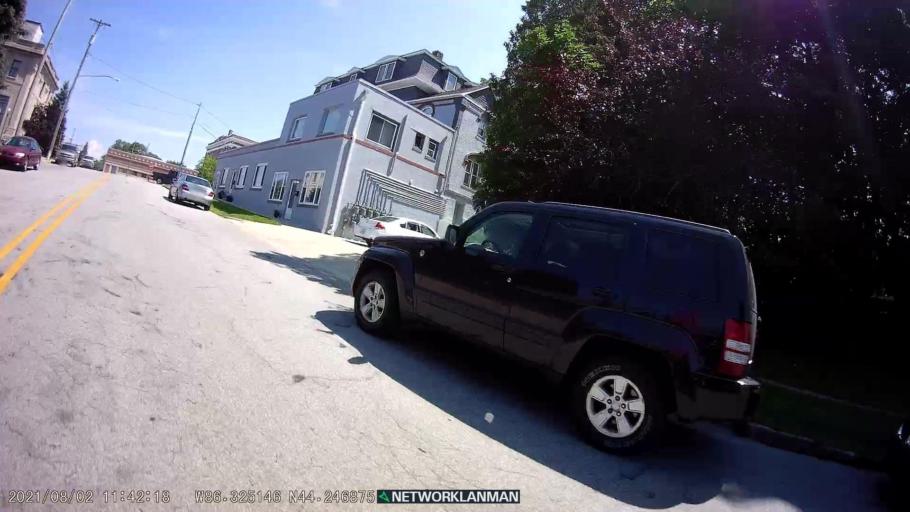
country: US
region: Michigan
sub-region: Manistee County
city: Manistee
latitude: 44.2469
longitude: -86.3249
